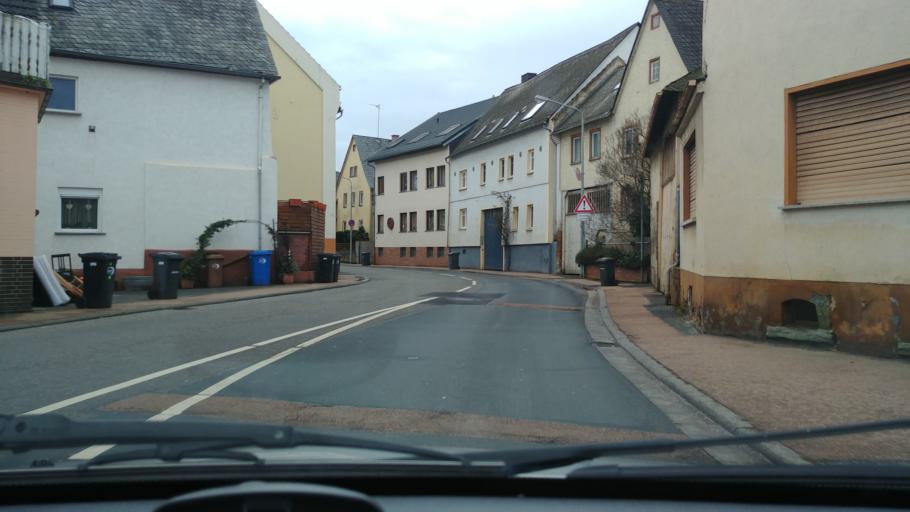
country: DE
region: Hesse
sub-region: Regierungsbezirk Giessen
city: Villmar
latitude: 50.3292
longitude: 8.1776
